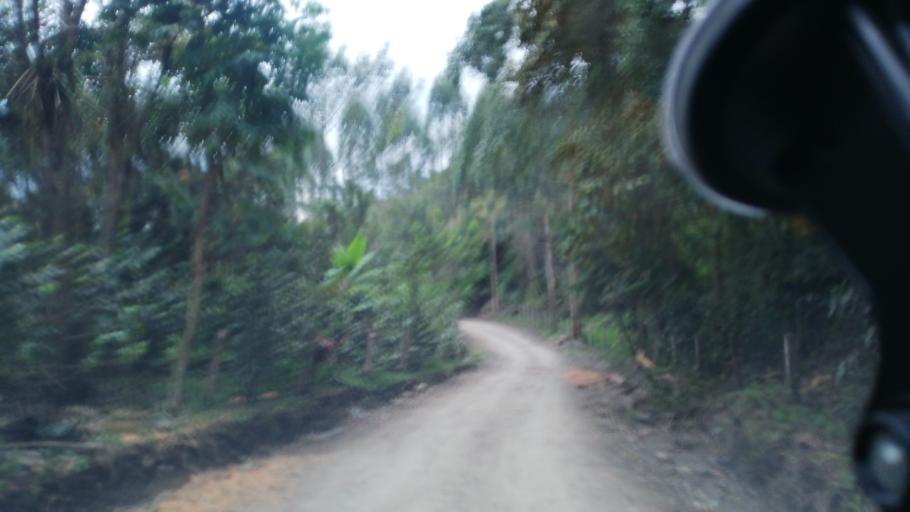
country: CO
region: Cundinamarca
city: Pacho
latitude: 5.1577
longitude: -74.2529
